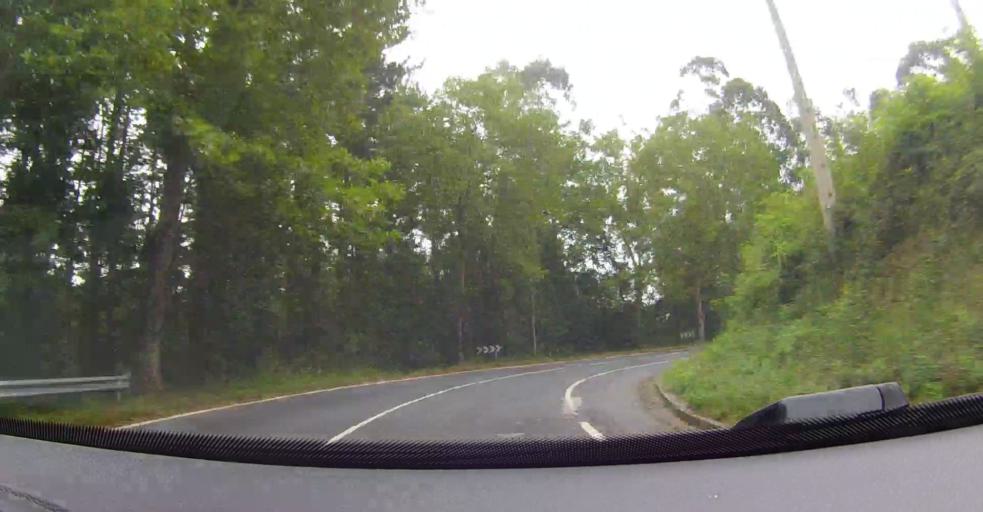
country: ES
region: Basque Country
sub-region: Bizkaia
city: Balmaseda
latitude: 43.2449
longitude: -3.2552
